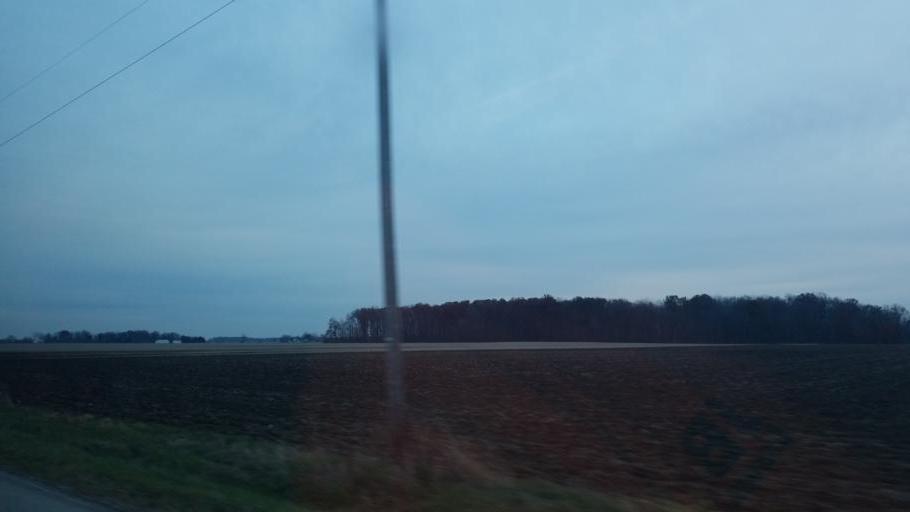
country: US
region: Indiana
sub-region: Adams County
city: Decatur
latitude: 40.7889
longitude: -84.9145
